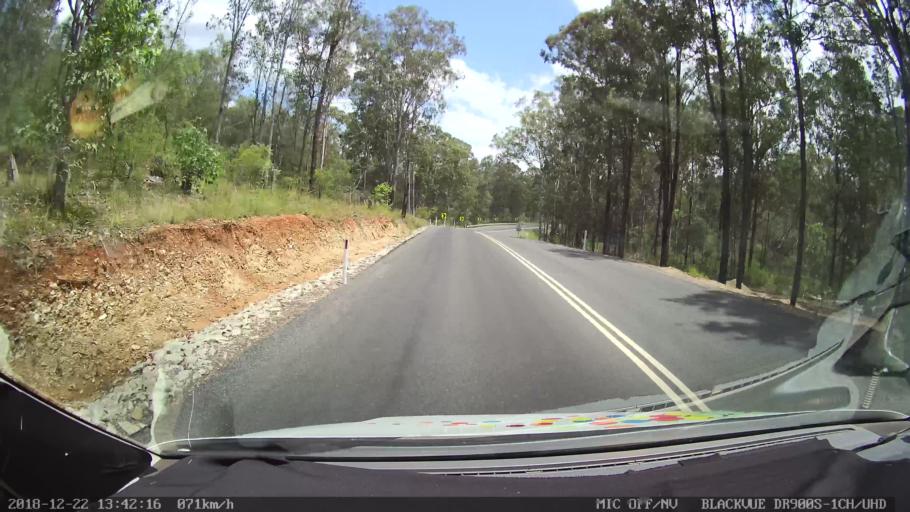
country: AU
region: New South Wales
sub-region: Clarence Valley
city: Coutts Crossing
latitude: -29.9216
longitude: 152.7545
